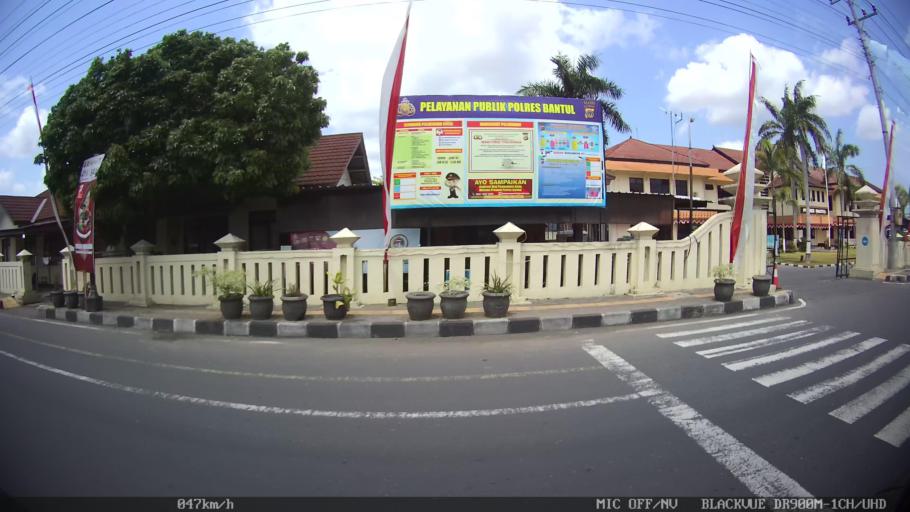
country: ID
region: Daerah Istimewa Yogyakarta
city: Bantul
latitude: -7.8892
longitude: 110.3273
